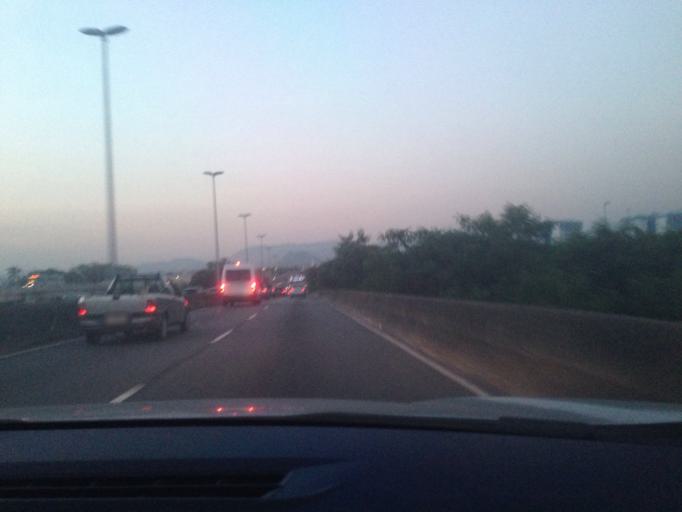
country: BR
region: Rio de Janeiro
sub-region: Sao Joao De Meriti
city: Sao Joao de Meriti
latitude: -22.9754
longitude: -43.3639
